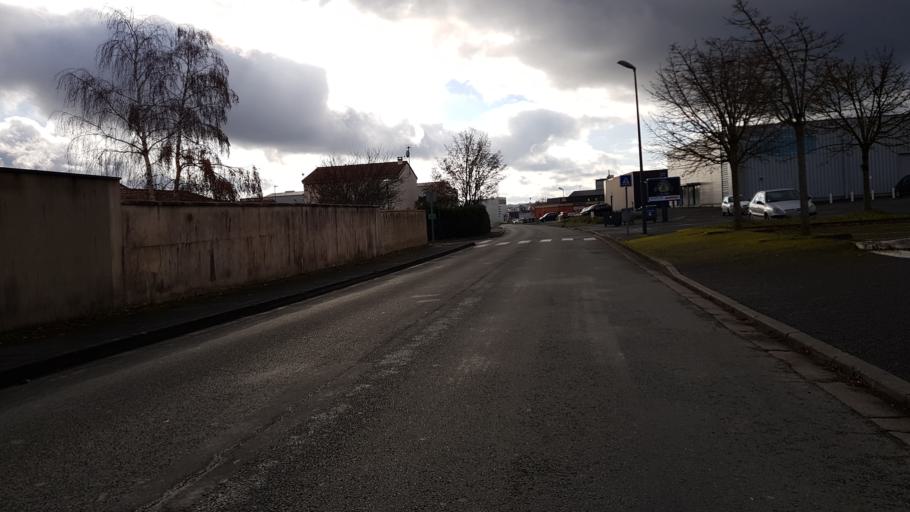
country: FR
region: Poitou-Charentes
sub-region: Departement de la Vienne
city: Chasseneuil-du-Poitou
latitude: 46.6517
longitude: 0.3660
